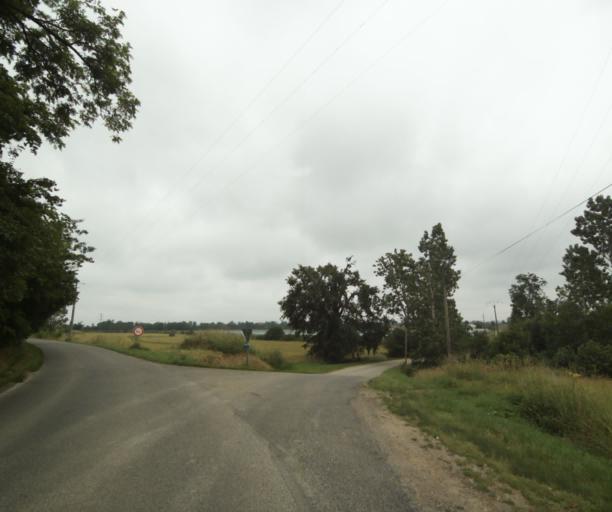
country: FR
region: Midi-Pyrenees
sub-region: Departement du Tarn-et-Garonne
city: Montbeton
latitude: 43.9920
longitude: 1.3060
